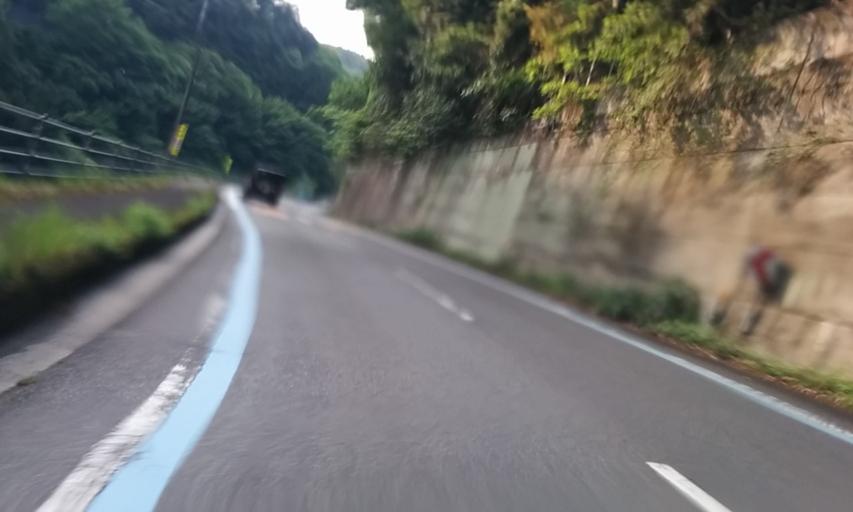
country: JP
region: Ehime
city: Saijo
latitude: 33.8728
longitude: 133.1758
